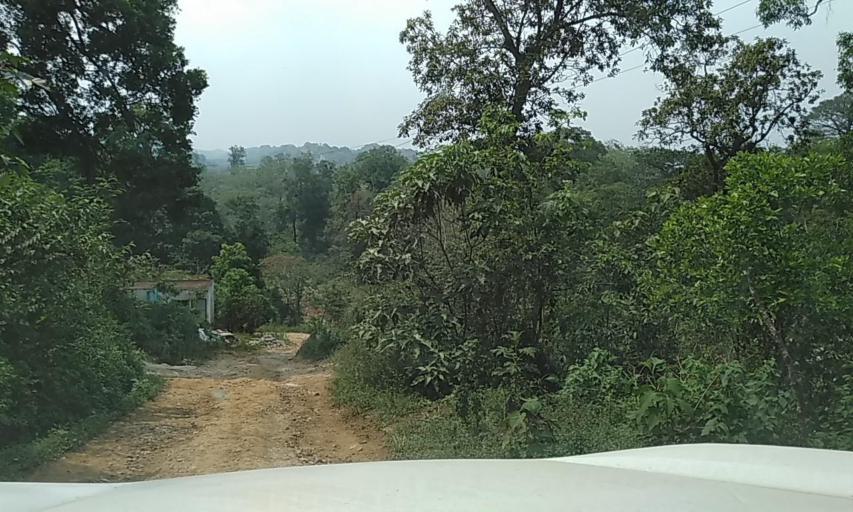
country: MX
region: Veracruz
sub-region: Jilotepec
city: El Pueblito (Garbanzal)
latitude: 19.5759
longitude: -96.8935
